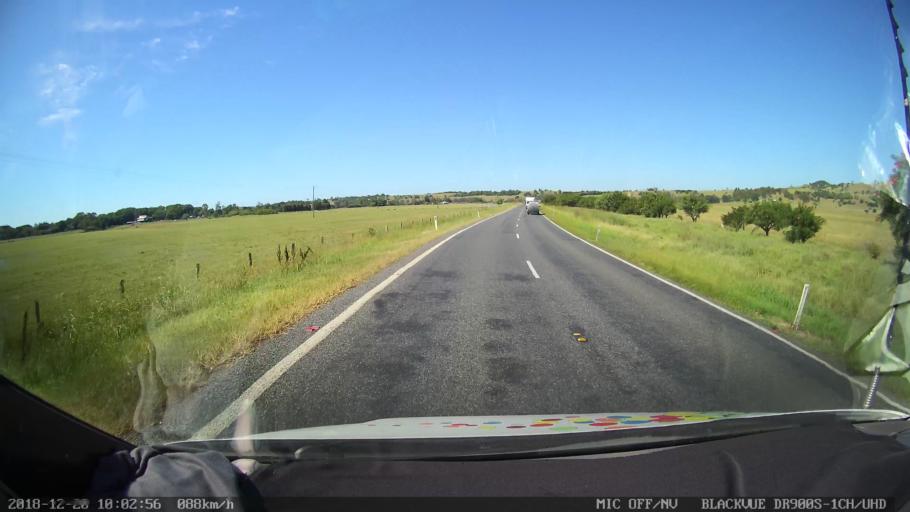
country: AU
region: New South Wales
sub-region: Lismore Municipality
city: East Lismore
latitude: -28.8641
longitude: 153.2602
